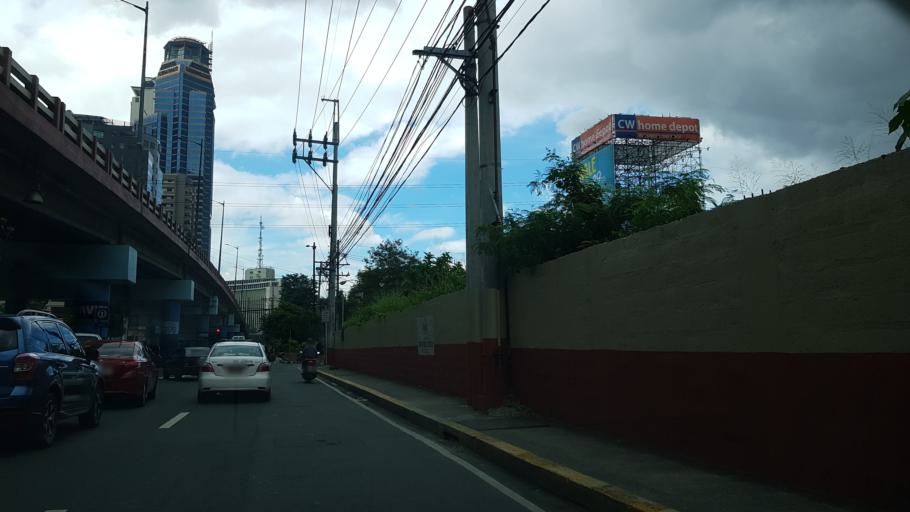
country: PH
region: Metro Manila
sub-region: Pasig
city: Pasig City
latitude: 14.5834
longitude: 121.0639
